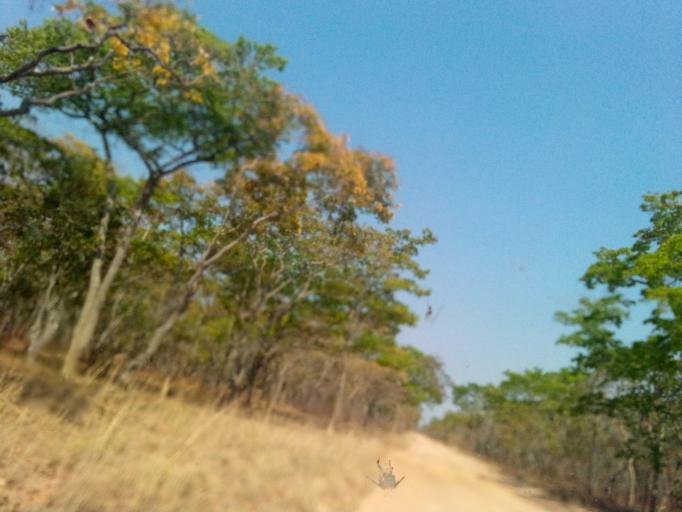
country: ZM
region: Northern
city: Mpika
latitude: -12.2419
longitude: 30.8550
